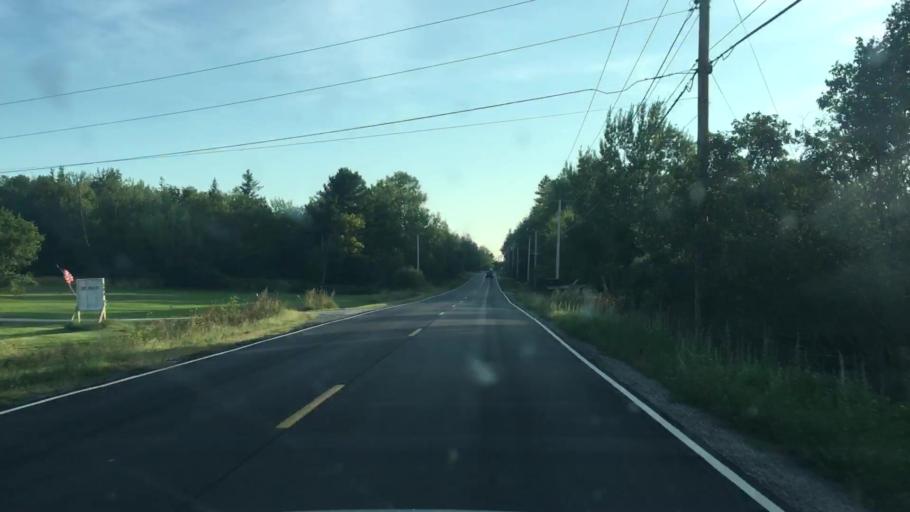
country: US
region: Maine
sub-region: Penobscot County
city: Hampden
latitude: 44.7215
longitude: -68.8841
